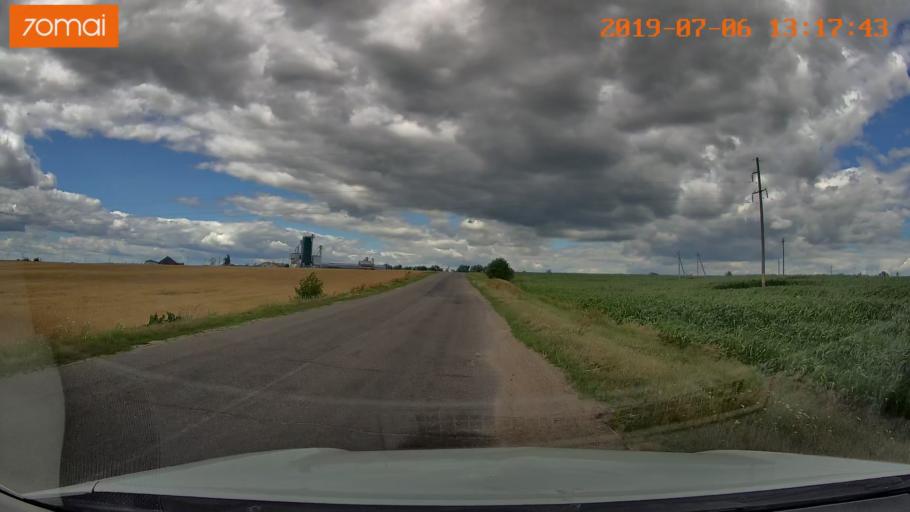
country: BY
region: Minsk
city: Enyerhyetykaw
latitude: 53.6667
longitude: 27.0136
